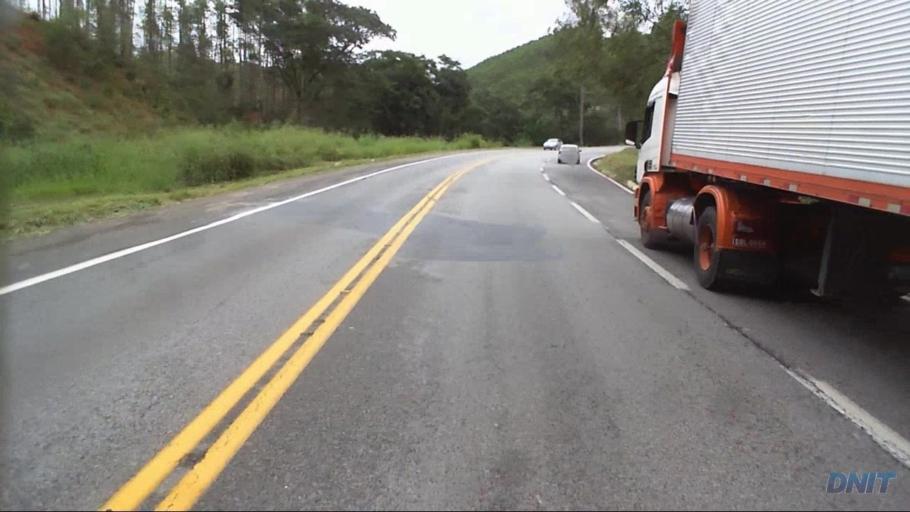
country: BR
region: Minas Gerais
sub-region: Joao Monlevade
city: Joao Monlevade
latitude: -19.8552
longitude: -43.2638
